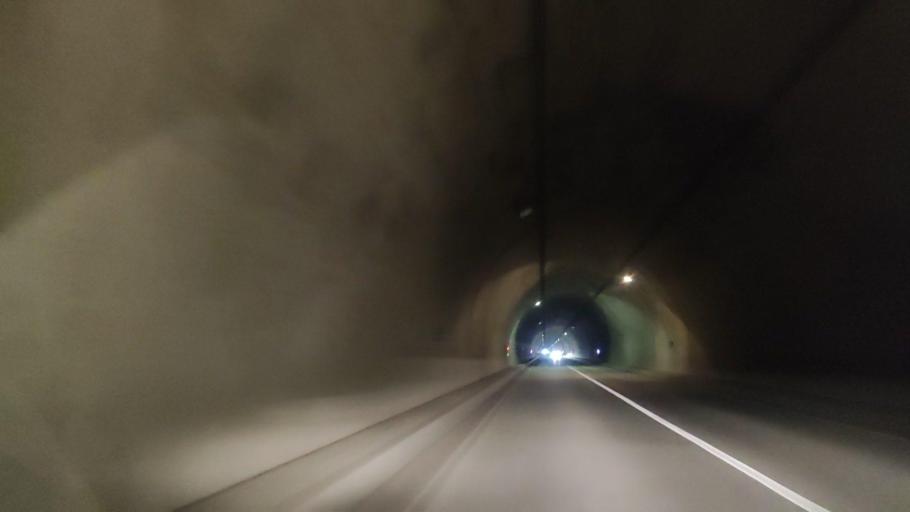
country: JP
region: Hokkaido
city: Iwamizawa
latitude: 43.0313
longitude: 142.0897
